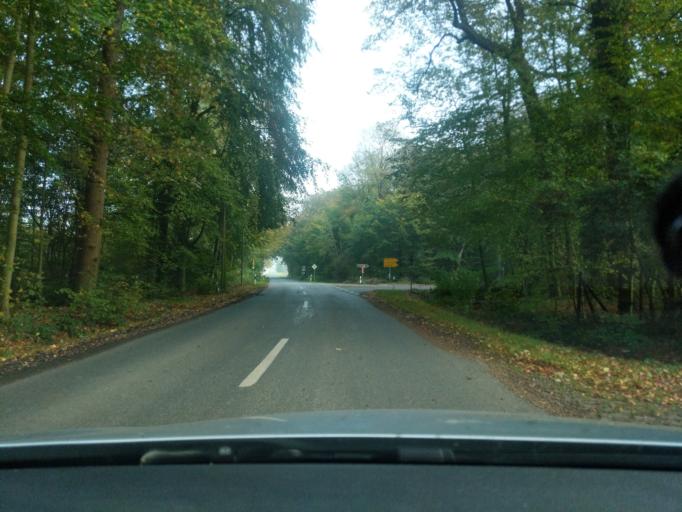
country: DE
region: Lower Saxony
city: Wanna
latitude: 53.7257
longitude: 8.7916
